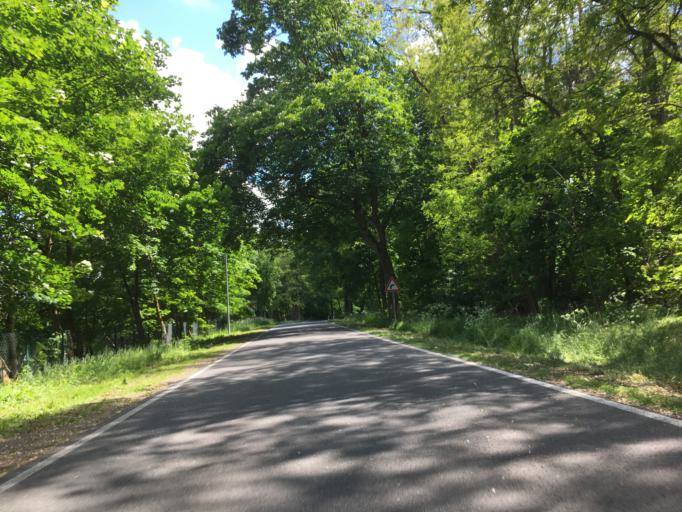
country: DE
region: Brandenburg
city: Protzel
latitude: 52.6824
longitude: 14.0073
